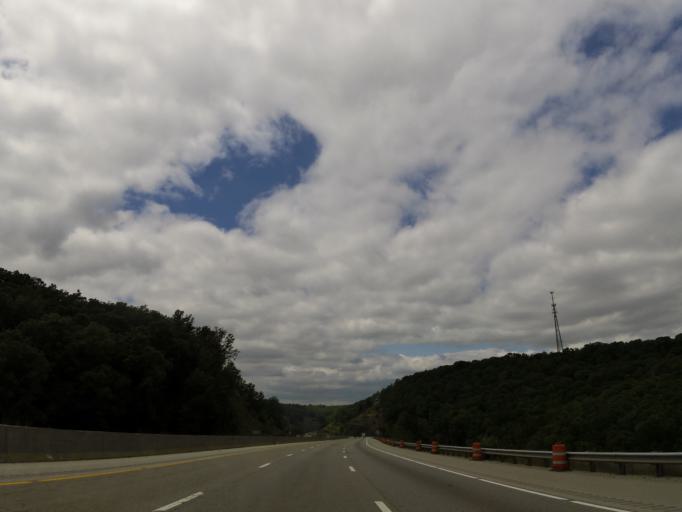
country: US
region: Kentucky
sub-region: Rockcastle County
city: Mount Vernon
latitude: 37.2322
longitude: -84.2259
